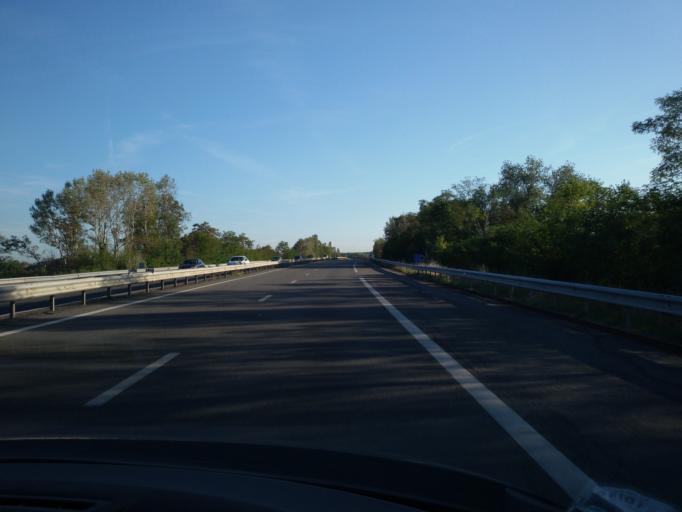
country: FR
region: Centre
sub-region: Departement du Cher
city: Orval
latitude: 46.7761
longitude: 2.4069
